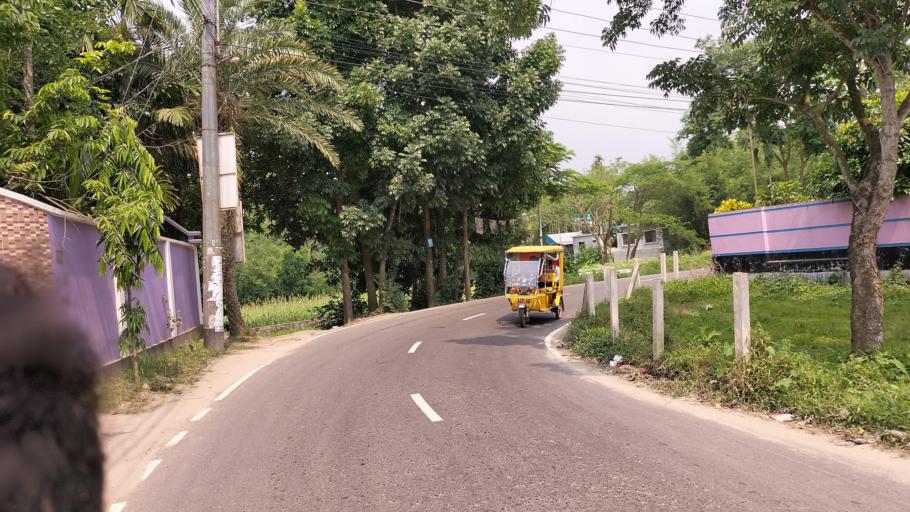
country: BD
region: Dhaka
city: Azimpur
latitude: 23.7015
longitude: 90.2914
